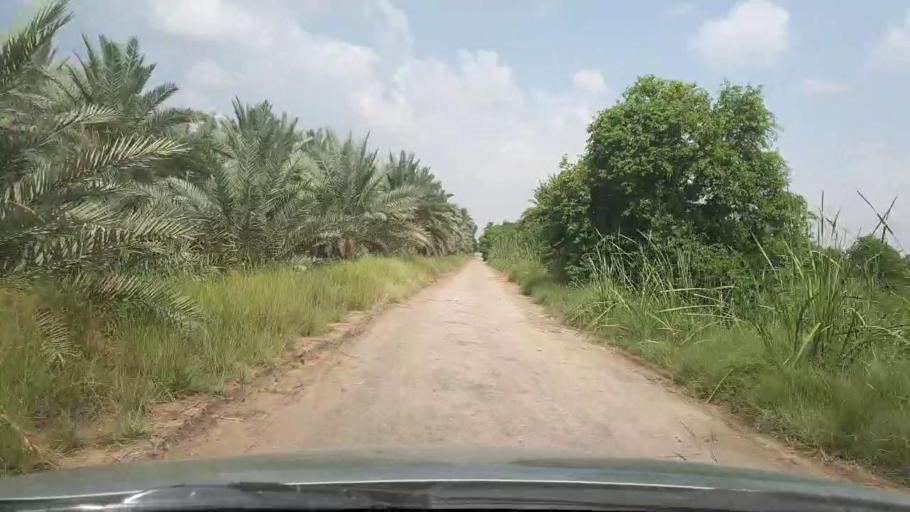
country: PK
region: Sindh
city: Khairpur
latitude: 27.4676
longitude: 68.7719
